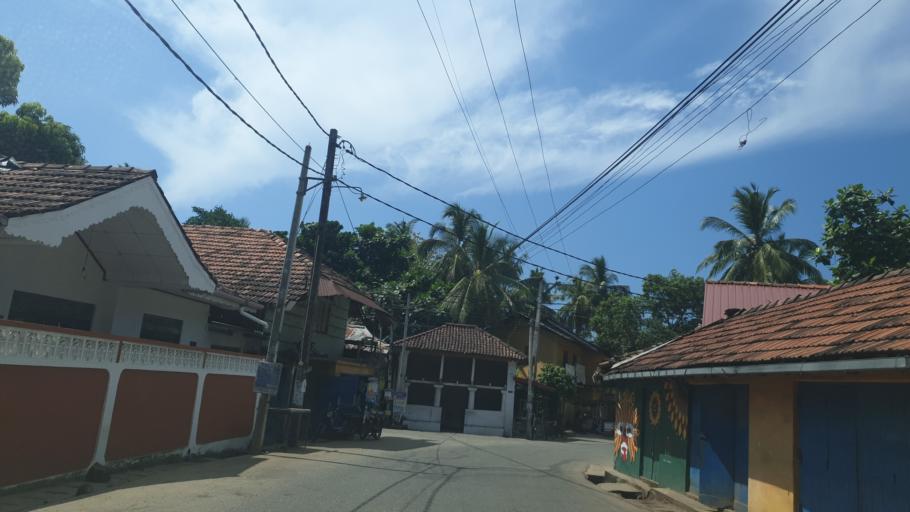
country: LK
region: Southern
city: Matara
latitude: 5.9760
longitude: 80.6578
